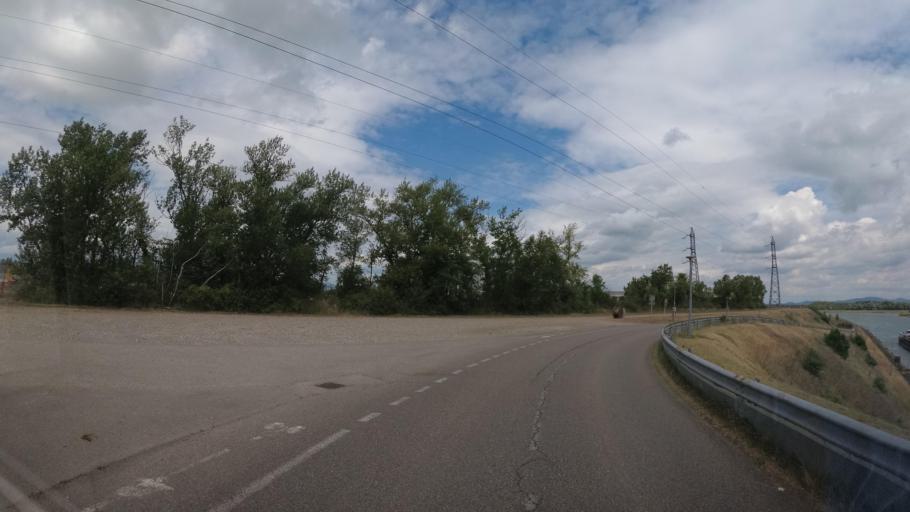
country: FR
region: Alsace
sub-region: Departement du Haut-Rhin
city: Fessenheim
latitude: 47.9118
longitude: 7.5712
